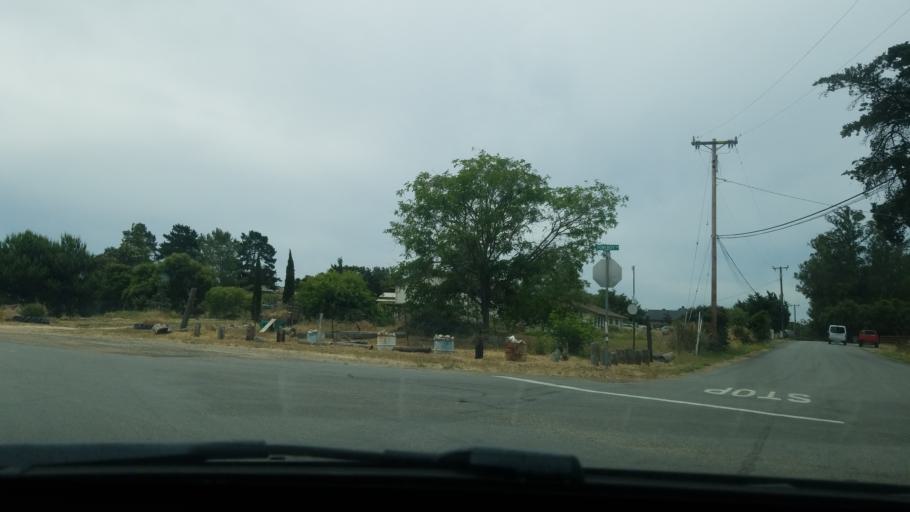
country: US
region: California
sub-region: San Luis Obispo County
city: Callender
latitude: 35.0687
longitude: -120.5420
